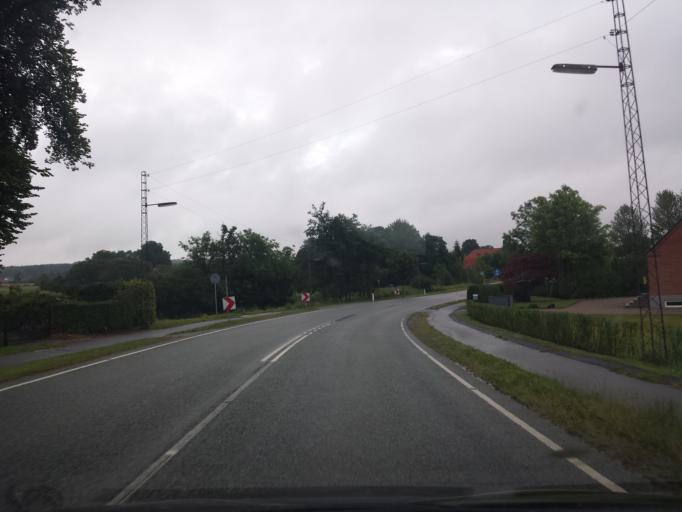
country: DK
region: South Denmark
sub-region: Sonderborg Kommune
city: Grasten
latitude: 54.9359
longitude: 9.6156
